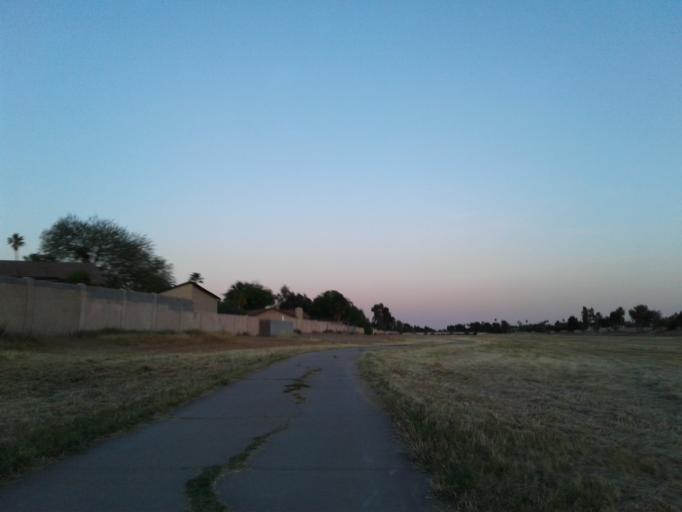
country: US
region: Arizona
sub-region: Maricopa County
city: Paradise Valley
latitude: 33.6031
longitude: -112.0031
